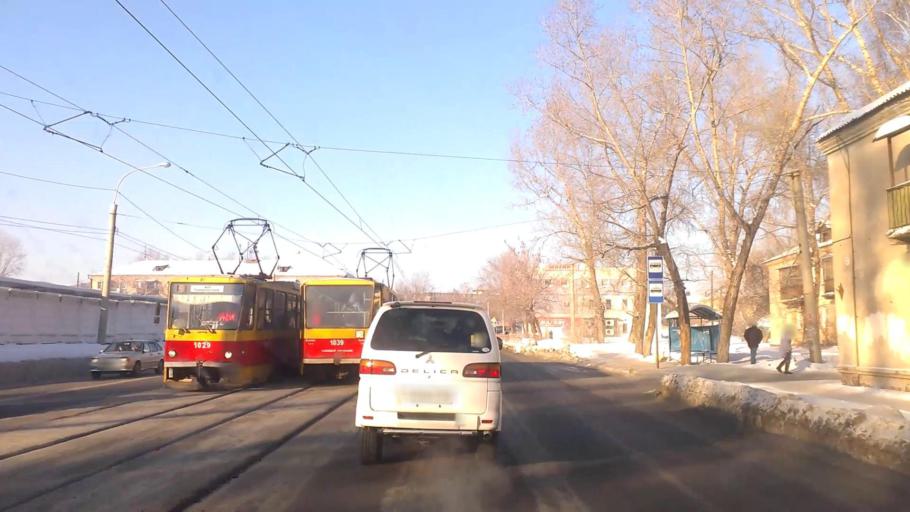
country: RU
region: Altai Krai
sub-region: Gorod Barnaulskiy
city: Barnaul
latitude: 53.3475
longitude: 83.7309
